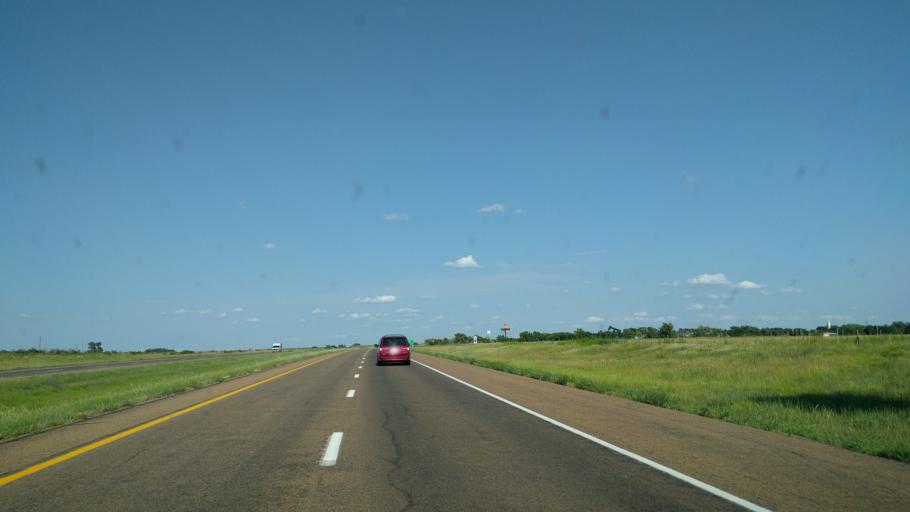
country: US
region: Kansas
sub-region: Ellis County
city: Ellis
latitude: 38.9501
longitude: -99.5713
